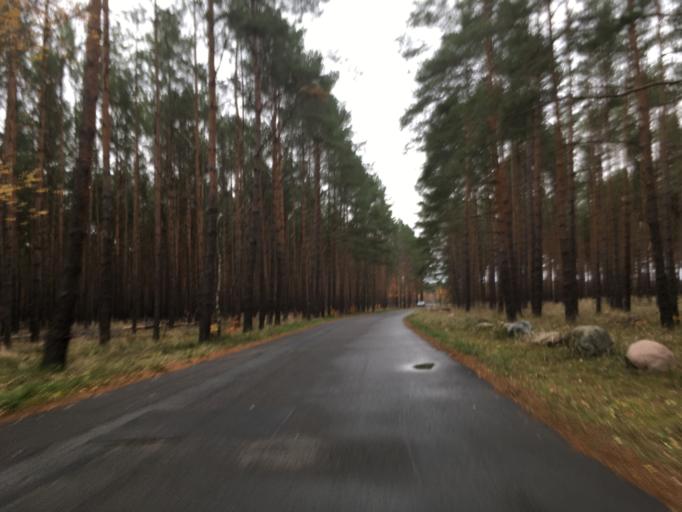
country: DE
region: Brandenburg
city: Mullrose
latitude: 52.2653
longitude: 14.4776
